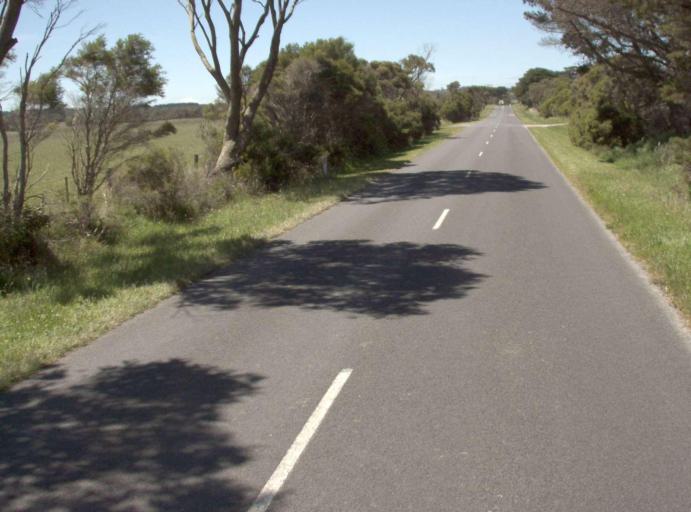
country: AU
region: Victoria
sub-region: Bass Coast
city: North Wonthaggi
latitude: -38.7999
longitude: 146.0860
